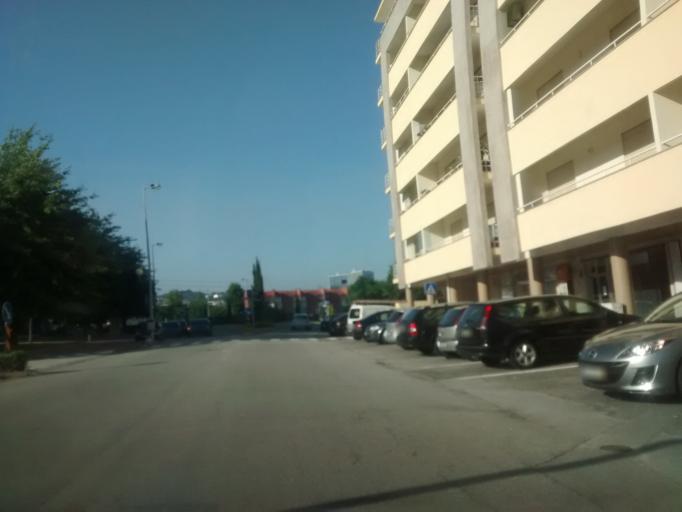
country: PT
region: Braga
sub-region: Braga
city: Braga
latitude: 41.5520
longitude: -8.4005
